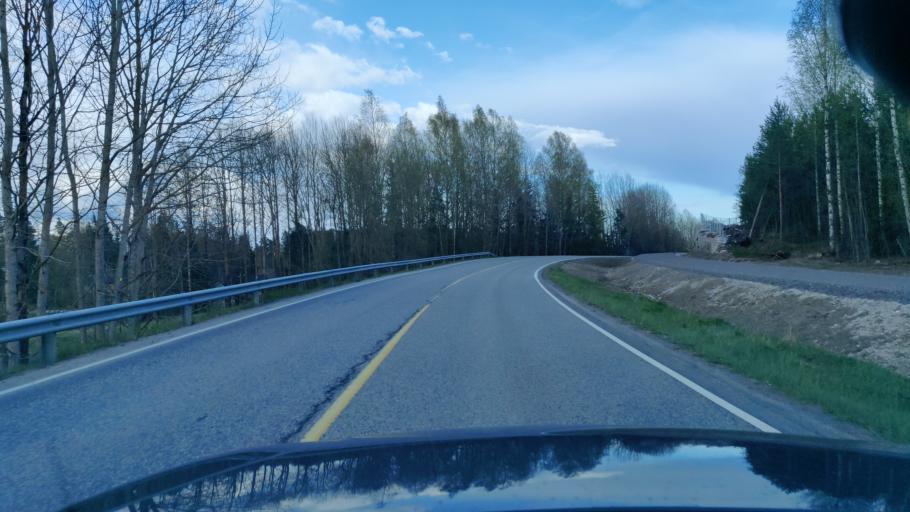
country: FI
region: Uusimaa
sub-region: Helsinki
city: Jaervenpaeae
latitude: 60.4788
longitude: 25.0619
